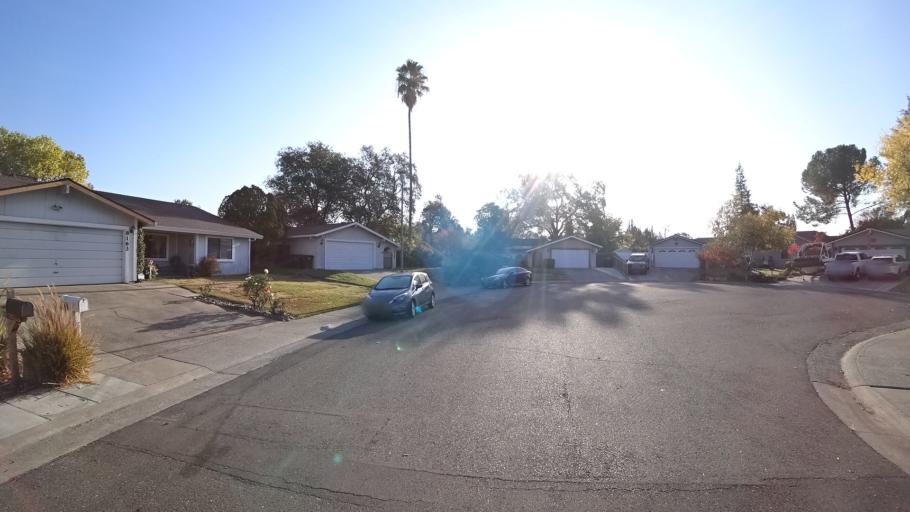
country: US
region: California
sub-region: Sacramento County
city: Citrus Heights
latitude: 38.6962
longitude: -121.2595
